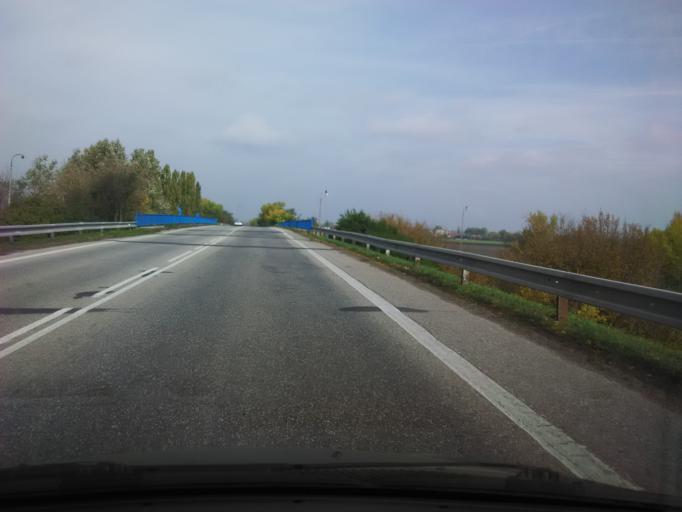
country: SK
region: Nitriansky
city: Komarno
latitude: 47.7765
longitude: 18.1601
